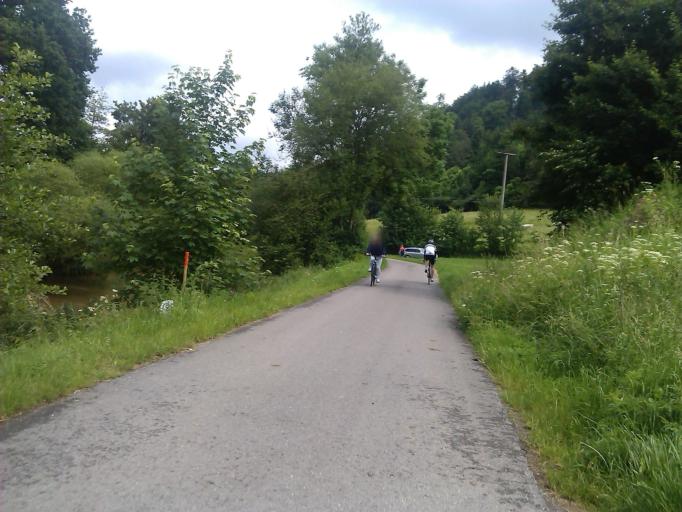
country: DE
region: Baden-Wuerttemberg
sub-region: Regierungsbezirk Stuttgart
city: Gaildorf
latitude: 48.9742
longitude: 9.7951
